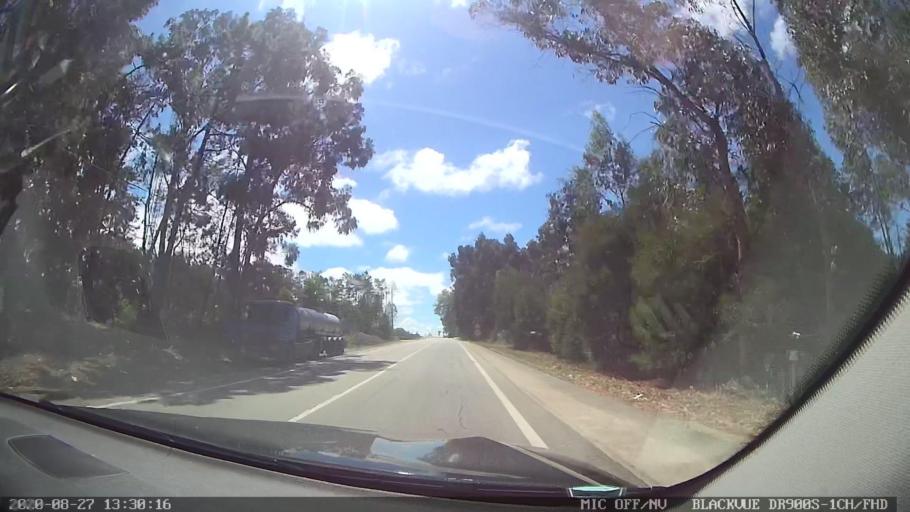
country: PT
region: Aveiro
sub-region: Vagos
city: Vagos
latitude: 40.5055
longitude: -8.6794
